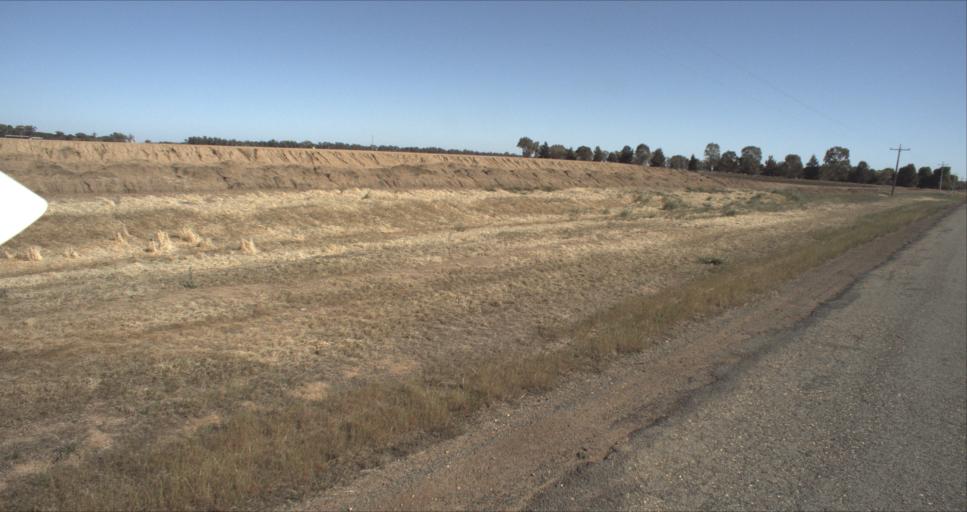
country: AU
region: New South Wales
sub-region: Leeton
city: Leeton
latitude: -34.5907
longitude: 146.2597
